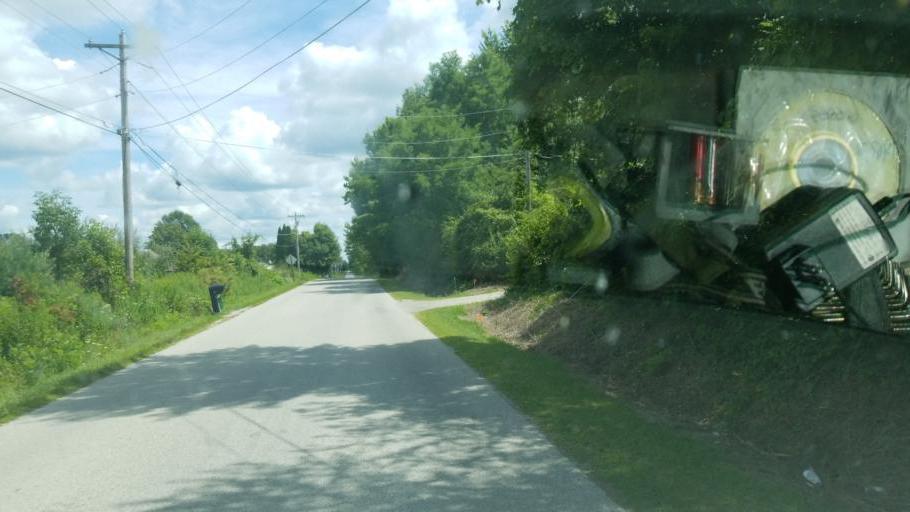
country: US
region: Ohio
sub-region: Knox County
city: Centerburg
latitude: 40.3658
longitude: -82.7706
